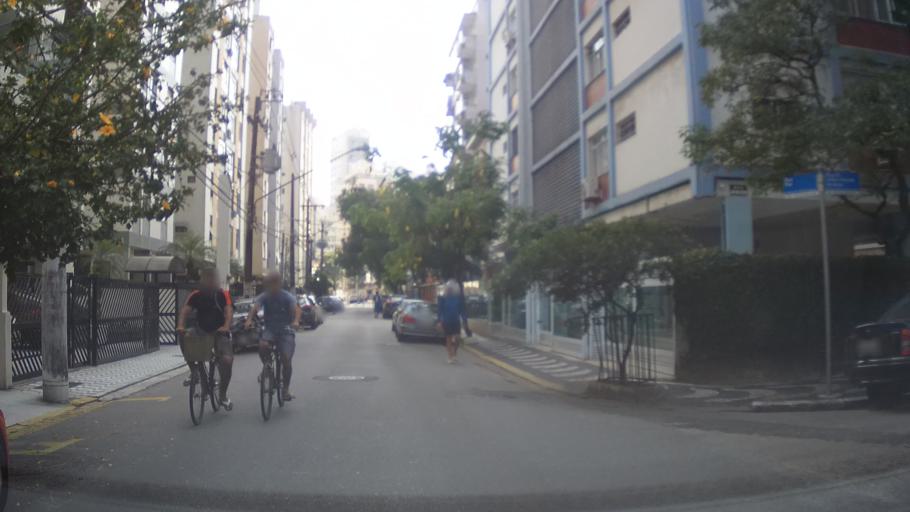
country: BR
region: Sao Paulo
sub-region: Santos
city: Santos
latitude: -23.9699
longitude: -46.3275
